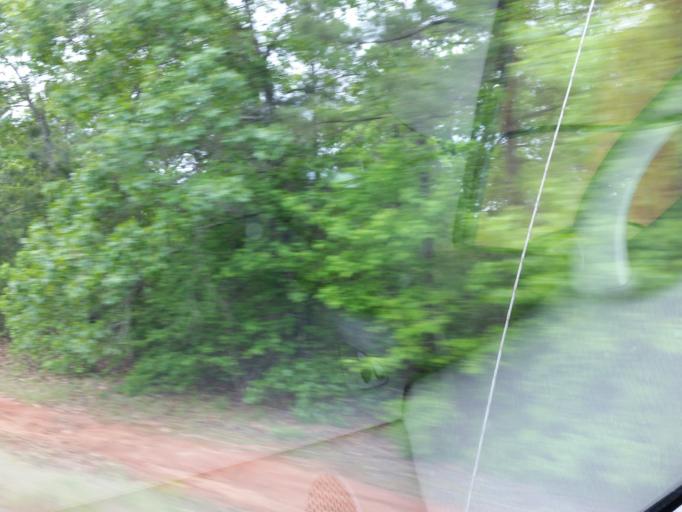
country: US
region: Georgia
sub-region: Crawford County
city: Knoxville
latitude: 32.6984
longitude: -83.9264
